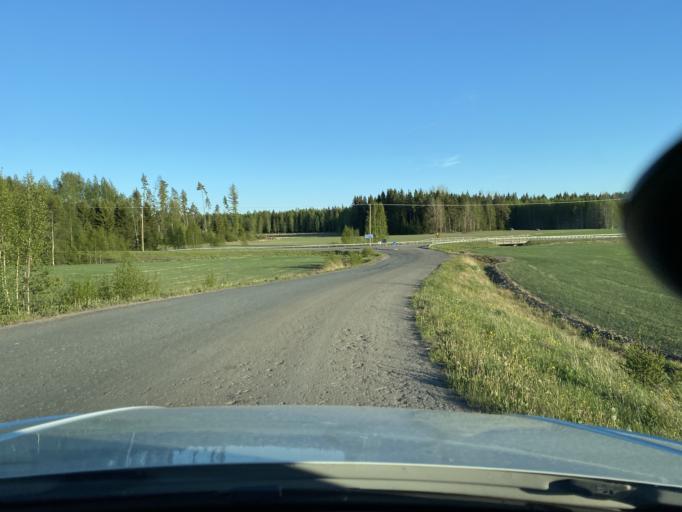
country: FI
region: Satakunta
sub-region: Rauma
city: Kiukainen
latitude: 61.1317
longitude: 21.9887
